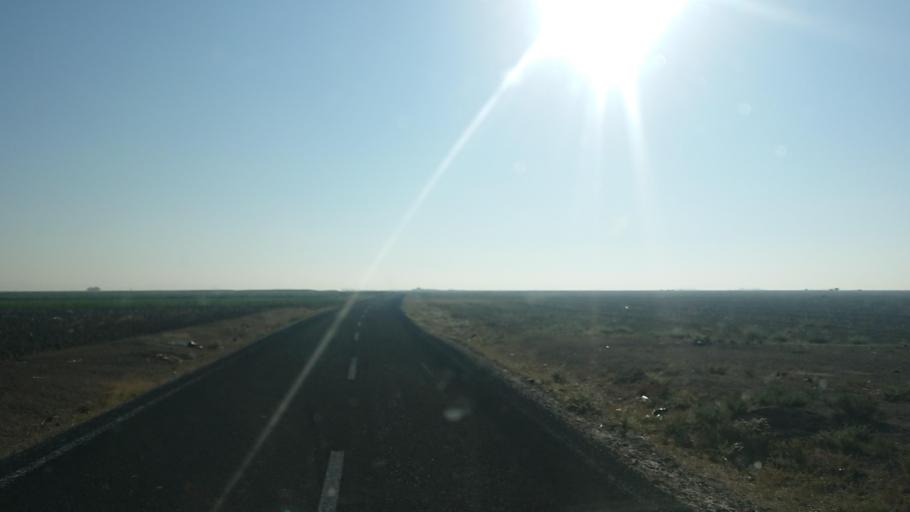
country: TR
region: Aksaray
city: Yesilova
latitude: 38.3877
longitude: 33.7858
